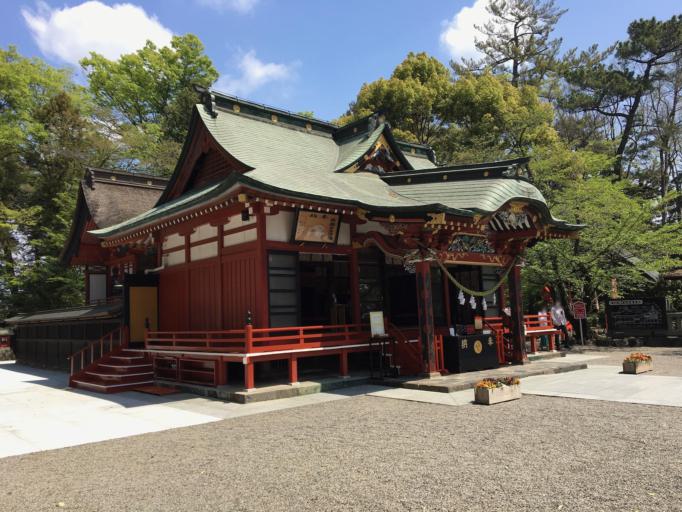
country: JP
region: Gunma
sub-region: Sawa-gun
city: Tamamura
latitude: 36.3050
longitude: 139.1087
